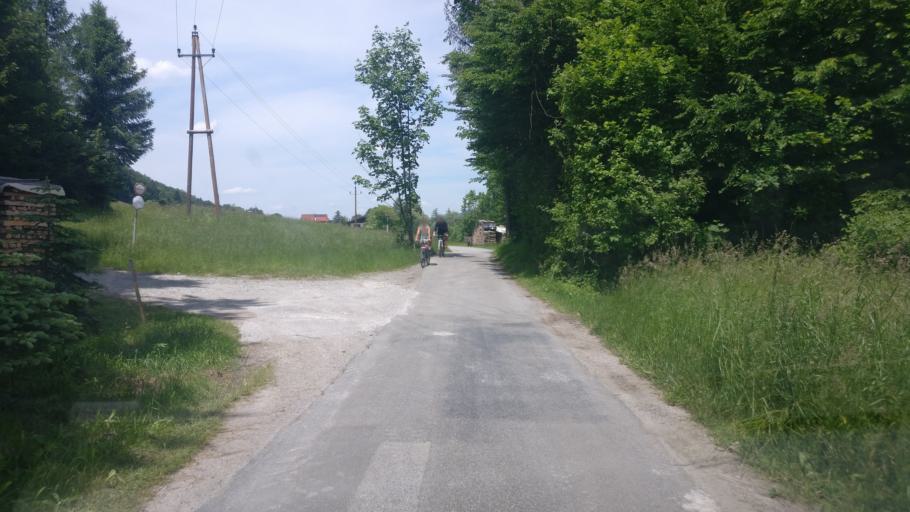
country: AT
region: Salzburg
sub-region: Politischer Bezirk Hallein
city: Kuchl
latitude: 47.6508
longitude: 13.1210
